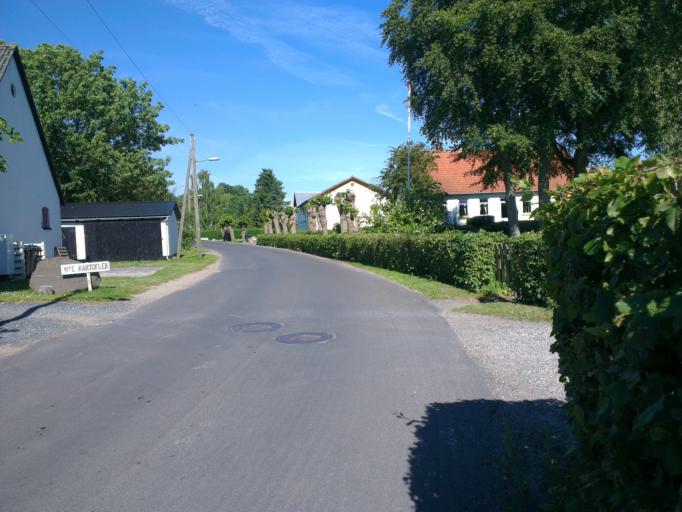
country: DK
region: Capital Region
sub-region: Frederikssund Kommune
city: Skibby
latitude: 55.7774
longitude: 11.9026
